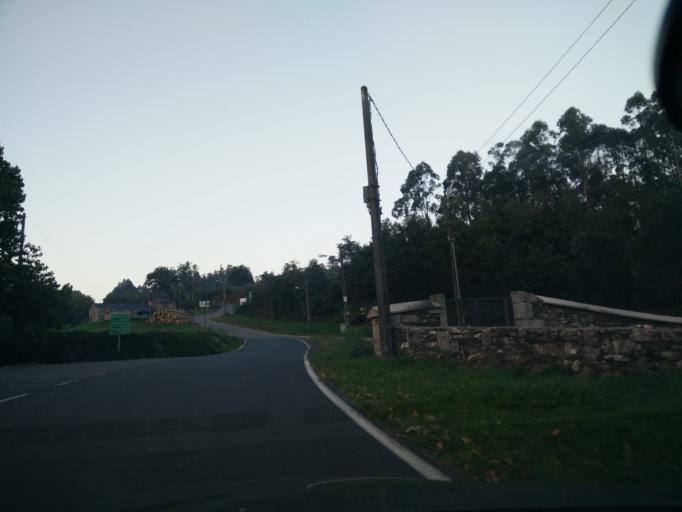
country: ES
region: Galicia
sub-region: Provincia da Coruna
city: Monfero
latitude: 43.3410
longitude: -8.0377
